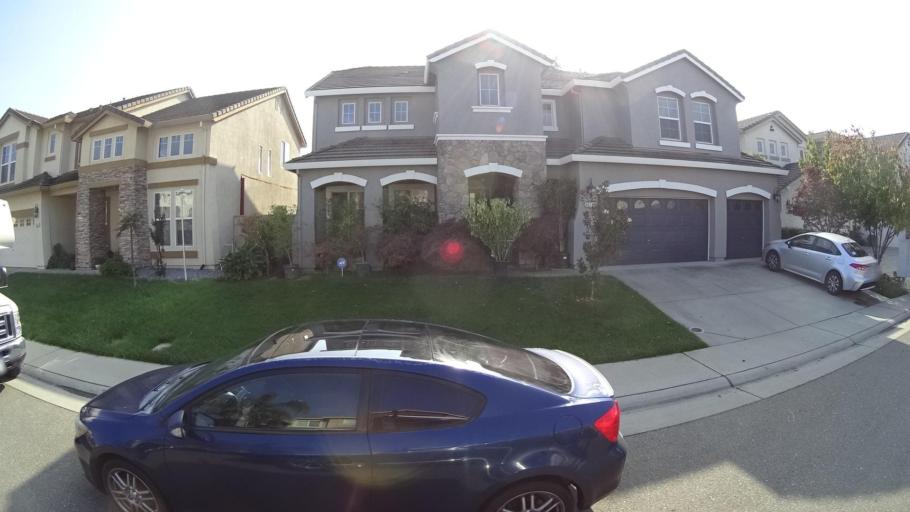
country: US
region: California
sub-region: Sacramento County
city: Elk Grove
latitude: 38.4204
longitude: -121.3379
